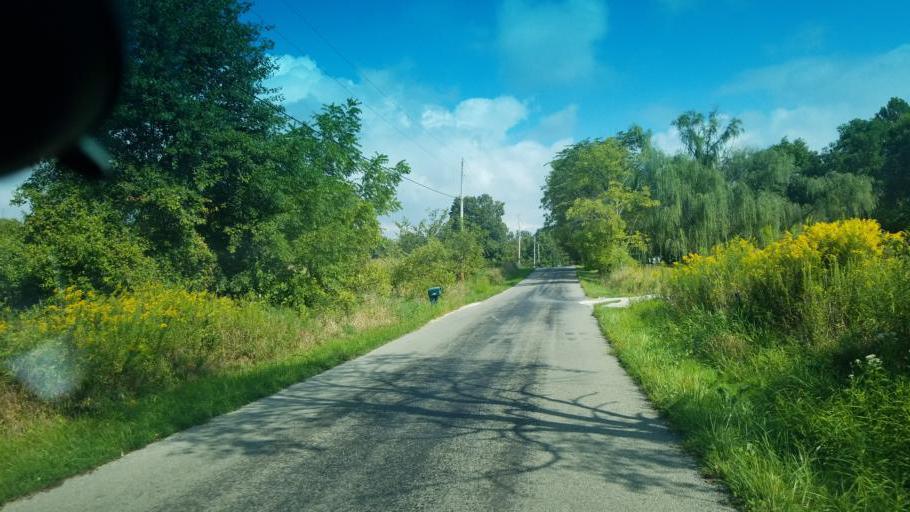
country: US
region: Ohio
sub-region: Licking County
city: Granville
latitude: 40.1751
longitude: -82.5629
